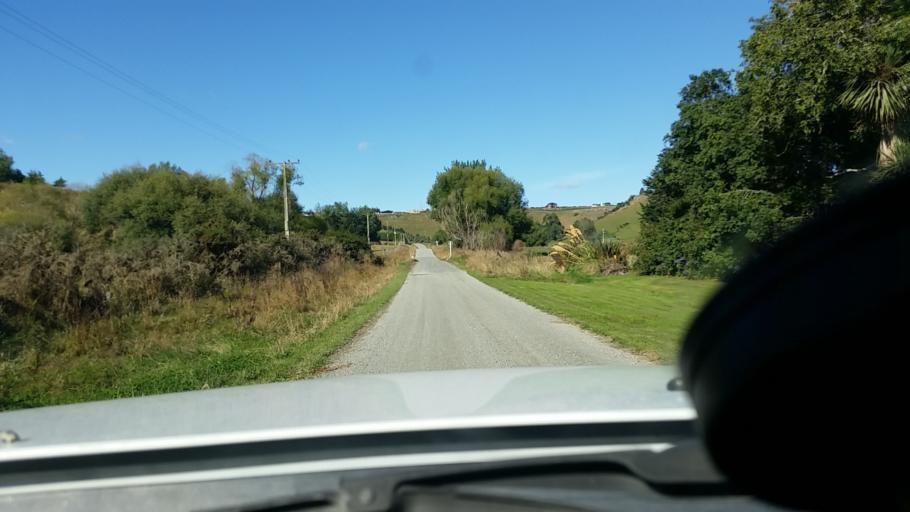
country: NZ
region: Canterbury
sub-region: Timaru District
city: Pleasant Point
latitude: -44.3445
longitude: 171.1592
